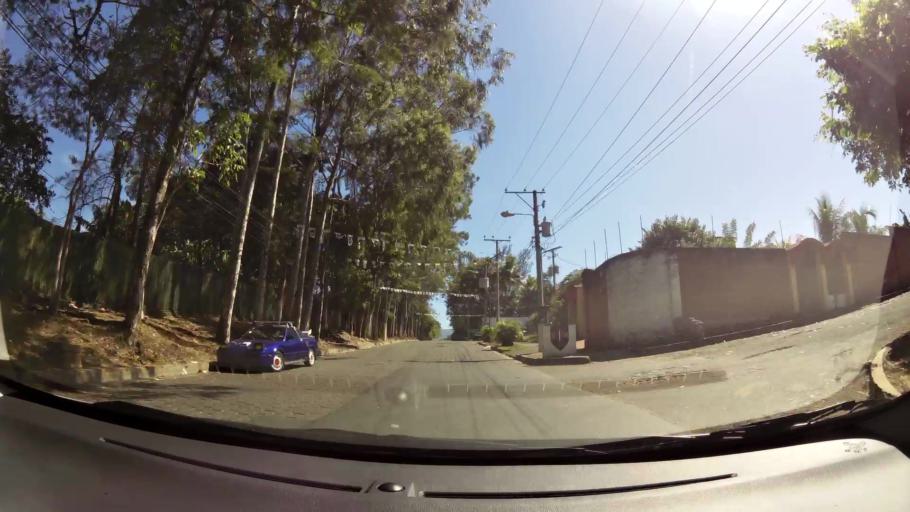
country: SV
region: Ahuachapan
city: Ahuachapan
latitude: 13.9228
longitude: -89.8436
